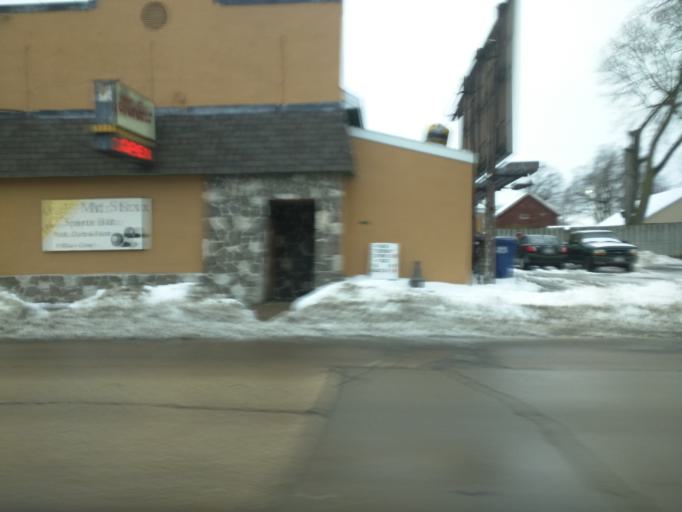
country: US
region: Wisconsin
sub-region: La Crosse County
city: La Crosse
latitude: 43.8015
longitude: -91.2426
